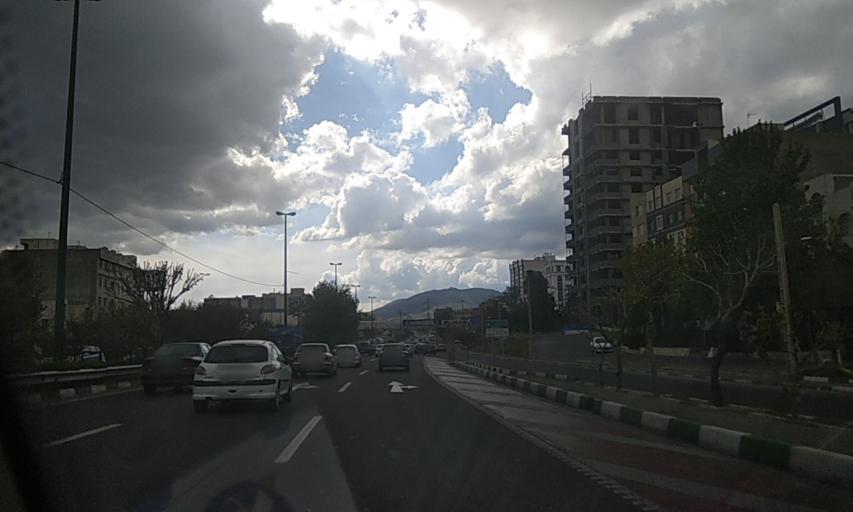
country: IR
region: Tehran
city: Tajrish
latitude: 35.7695
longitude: 51.3300
